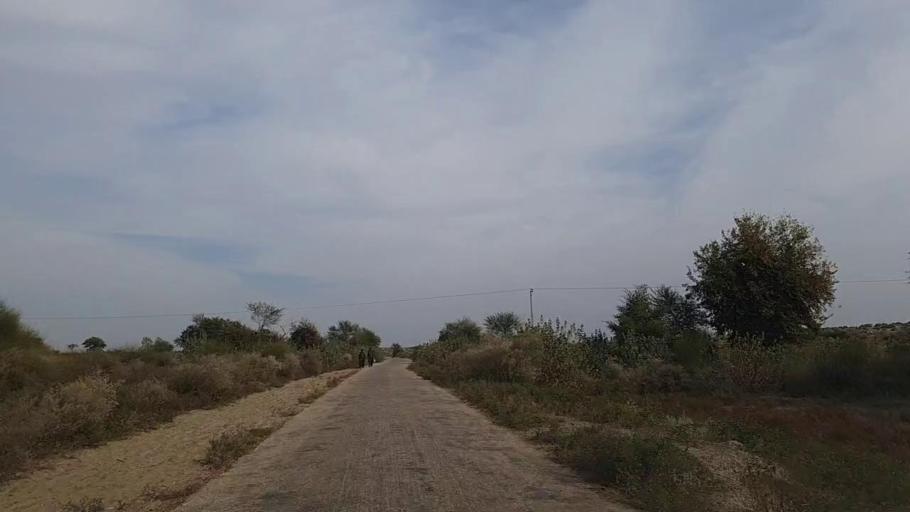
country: PK
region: Sindh
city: Jam Sahib
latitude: 26.4416
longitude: 68.6073
